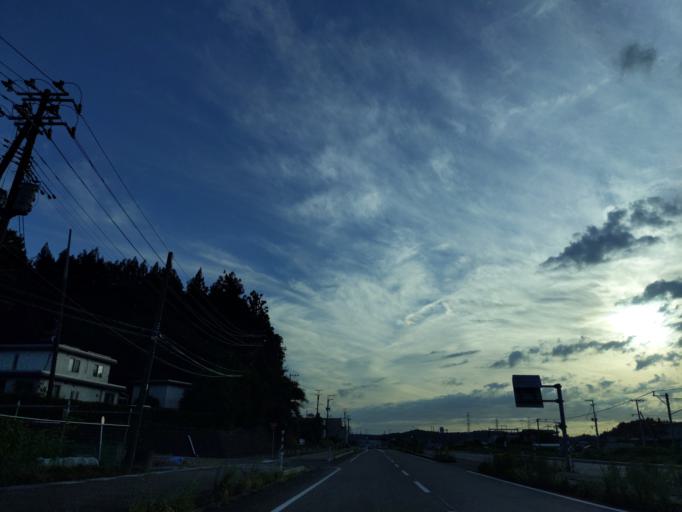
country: JP
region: Niigata
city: Kashiwazaki
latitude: 37.4513
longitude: 138.6487
